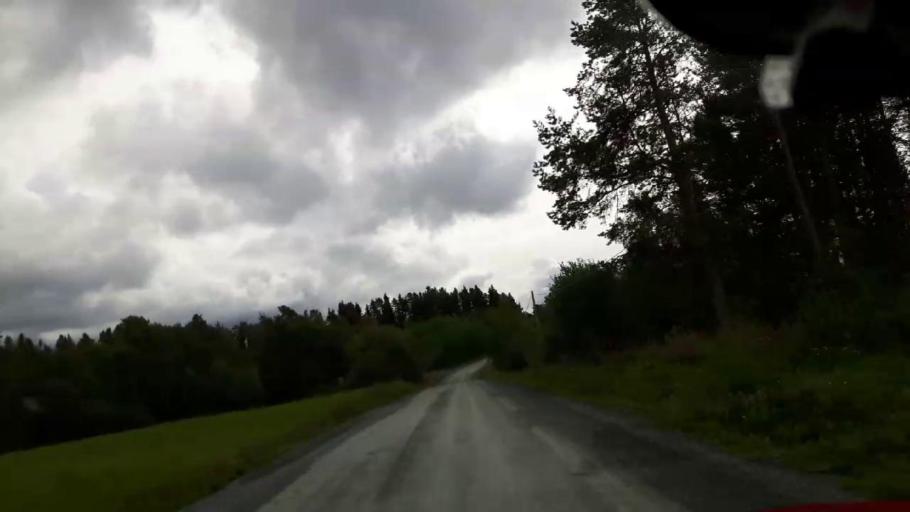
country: SE
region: Jaemtland
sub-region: Krokoms Kommun
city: Krokom
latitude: 63.5720
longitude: 14.2403
